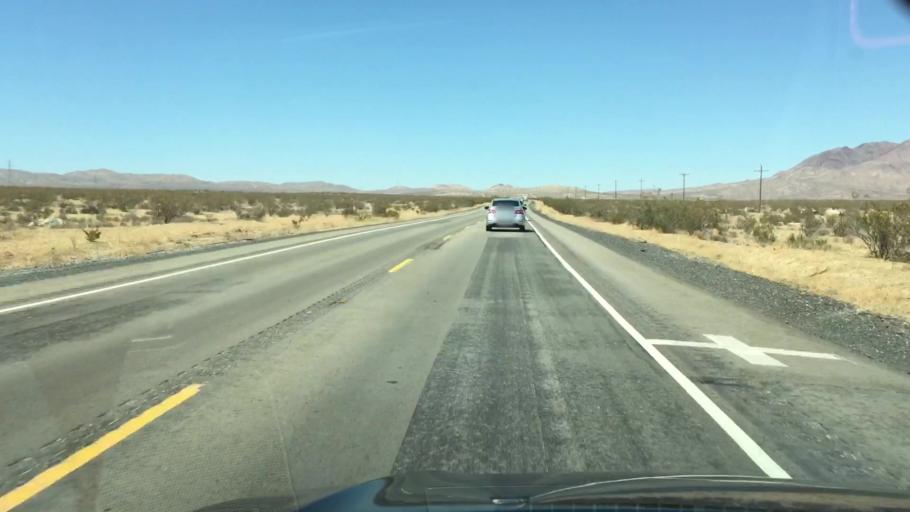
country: US
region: California
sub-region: Kern County
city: Boron
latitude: 35.2673
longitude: -117.6139
